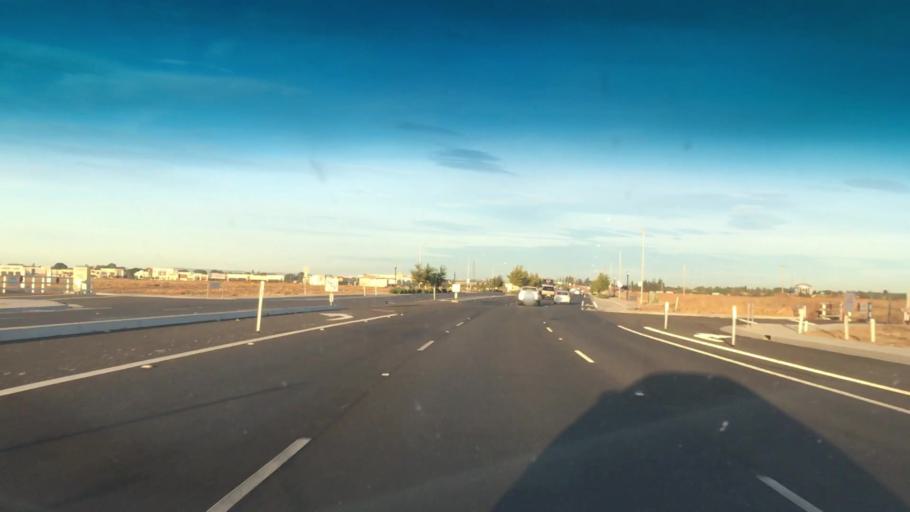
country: US
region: California
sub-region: Sacramento County
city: Parkway
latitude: 38.4644
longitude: -121.4821
